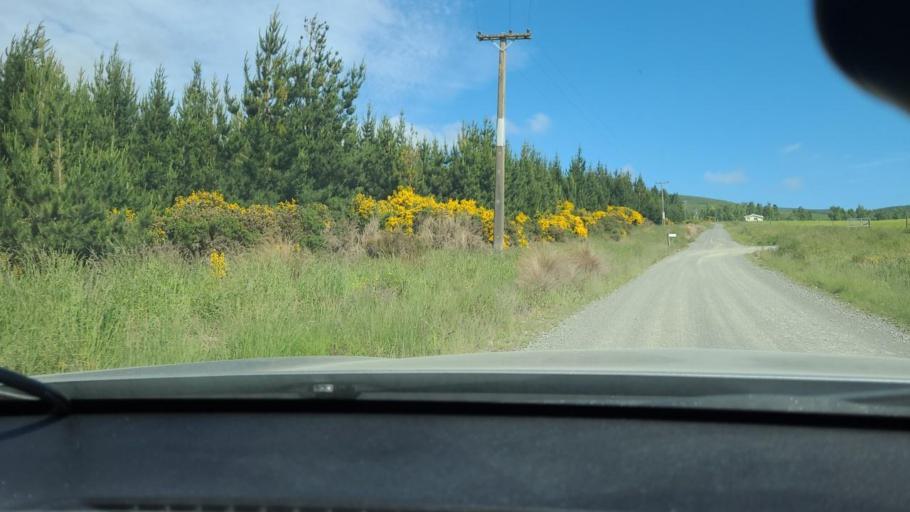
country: NZ
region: Southland
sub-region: Southland District
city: Winton
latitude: -45.8897
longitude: 168.0815
